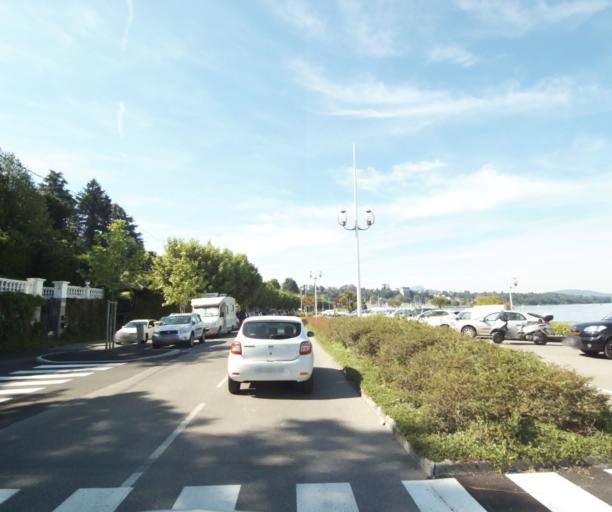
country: FR
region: Rhone-Alpes
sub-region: Departement de la Haute-Savoie
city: Thonon-les-Bains
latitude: 46.3833
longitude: 6.4831
